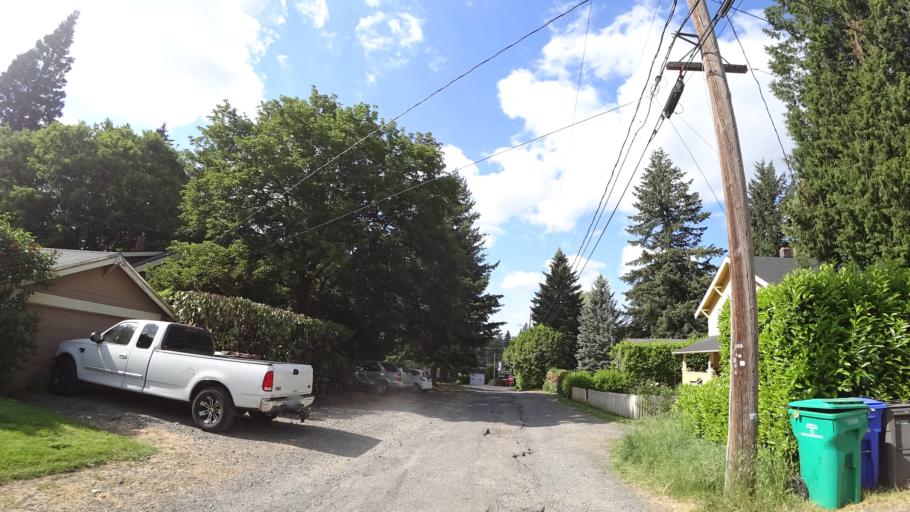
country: US
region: Oregon
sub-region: Washington County
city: Garden Home-Whitford
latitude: 45.4659
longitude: -122.7167
